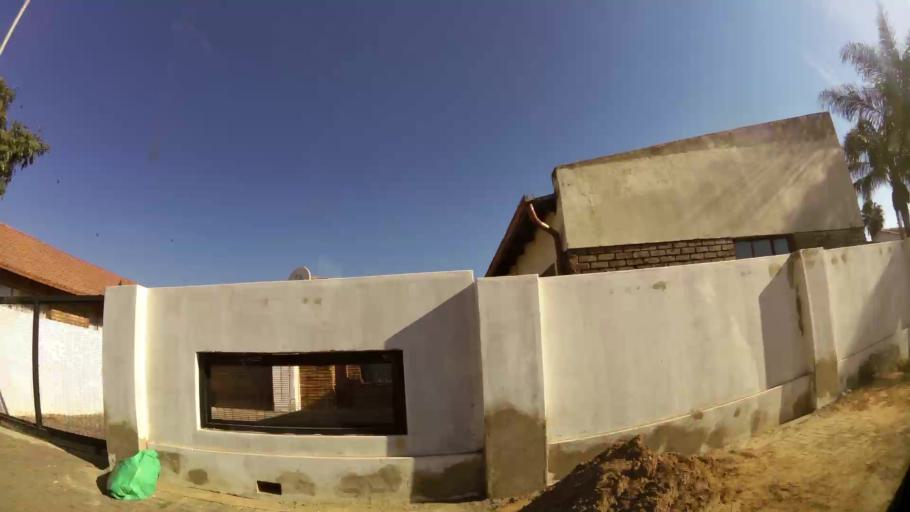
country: ZA
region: Gauteng
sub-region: City of Tshwane Metropolitan Municipality
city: Cullinan
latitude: -25.7202
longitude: 28.3790
